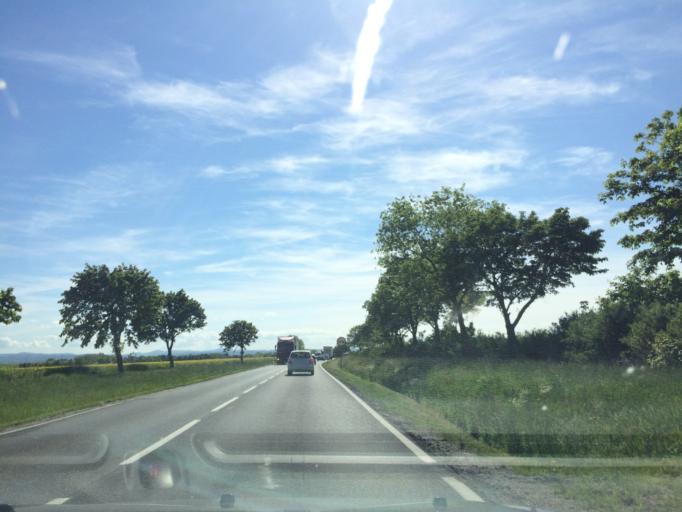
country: PL
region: Lower Silesian Voivodeship
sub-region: Powiat swidnicki
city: Zarow
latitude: 50.8884
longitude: 16.6033
